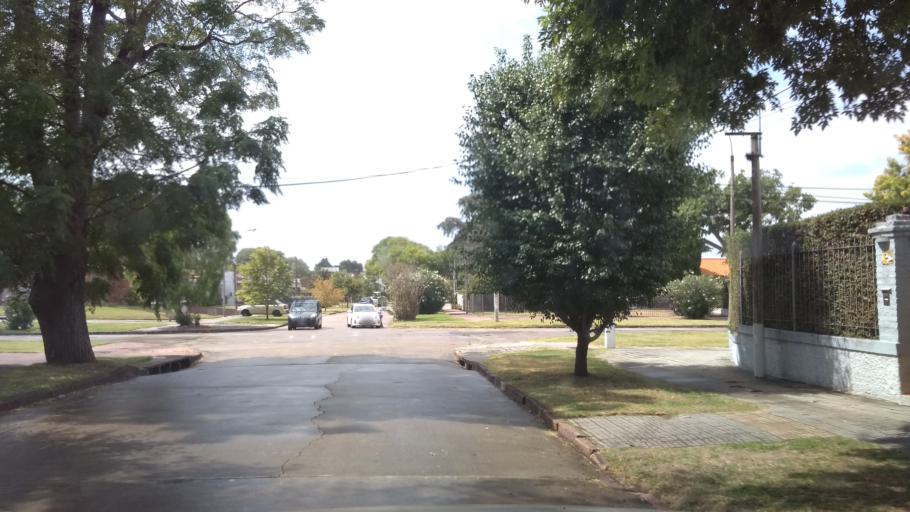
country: UY
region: Canelones
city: Paso de Carrasco
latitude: -34.8939
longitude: -56.0774
